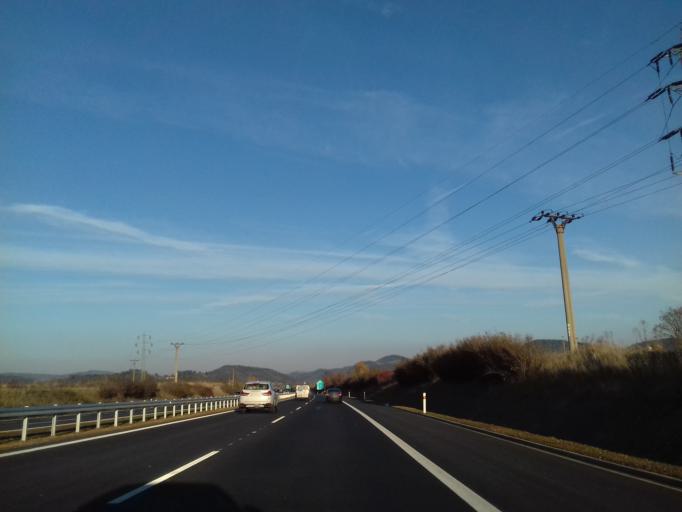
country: CZ
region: Central Bohemia
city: Zdice
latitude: 49.8954
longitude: 13.9488
